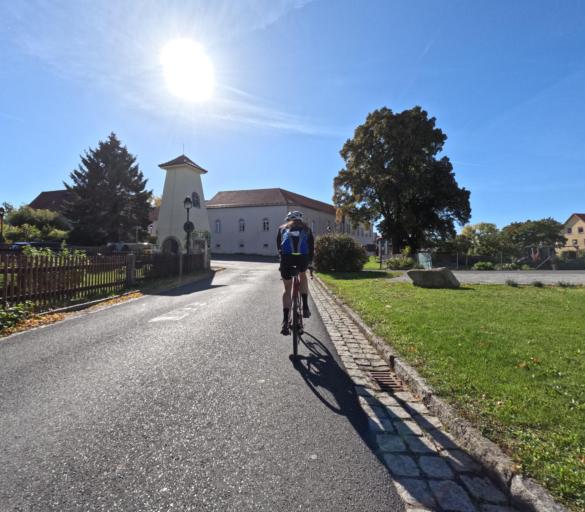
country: DE
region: Saxony
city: Moritzburg
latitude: 51.1219
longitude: 13.7207
